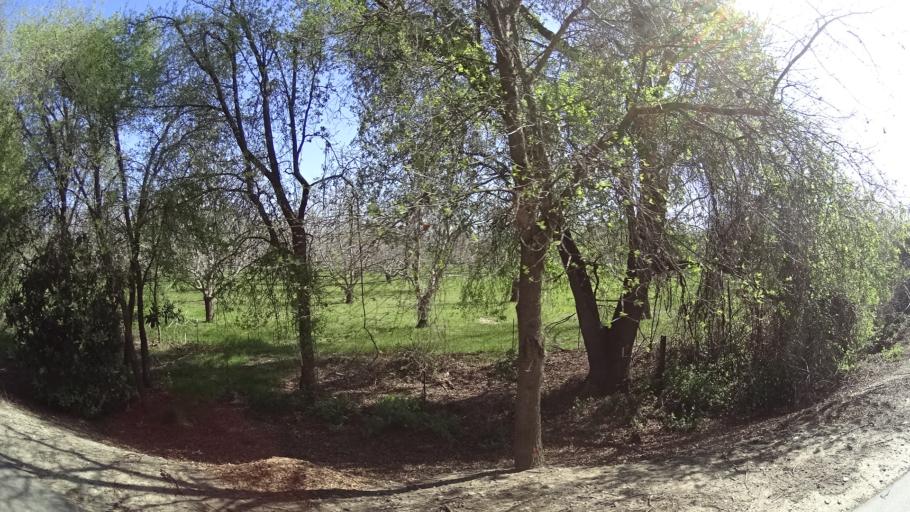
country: US
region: California
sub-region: Glenn County
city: Hamilton City
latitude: 39.7878
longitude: -122.0477
